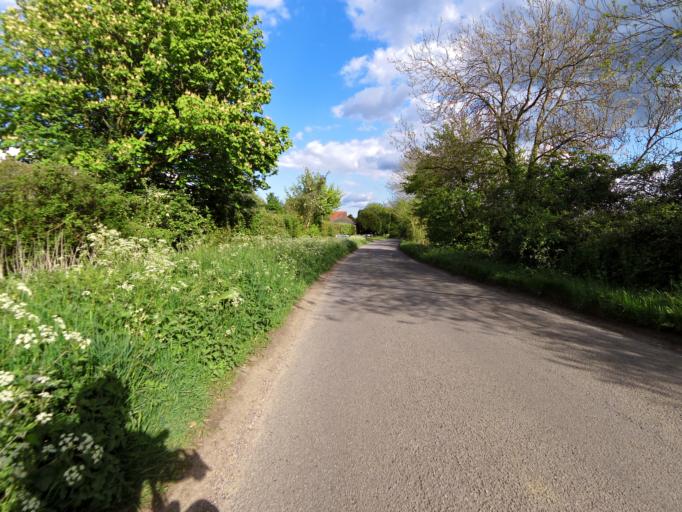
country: GB
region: England
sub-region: Suffolk
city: Stowmarket
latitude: 52.1985
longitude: 0.9531
